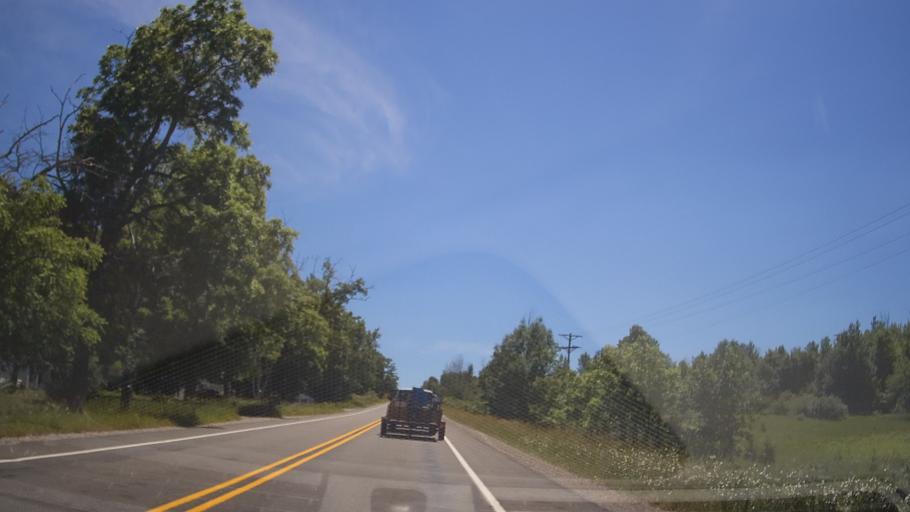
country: US
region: Michigan
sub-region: Grand Traverse County
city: Traverse City
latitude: 44.6222
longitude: -85.6965
